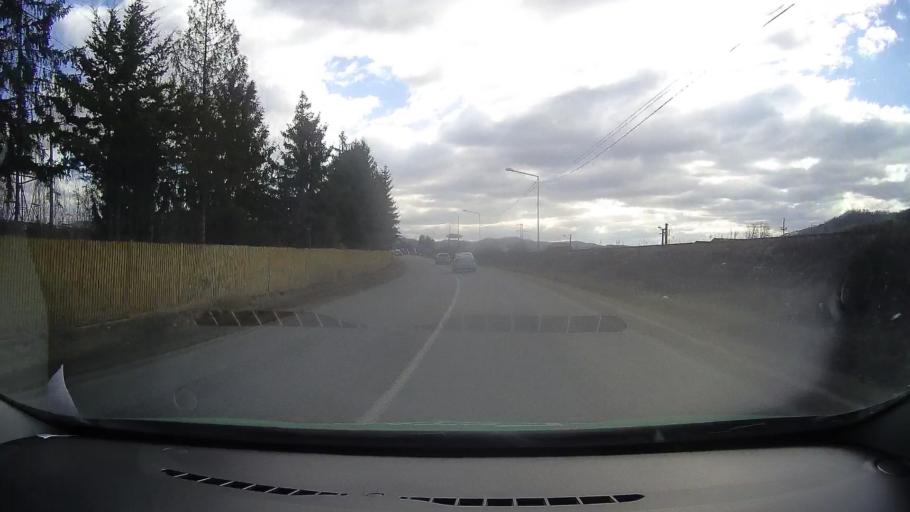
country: RO
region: Dambovita
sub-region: Oras Pucioasa
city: Pucioasa
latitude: 45.0836
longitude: 25.4219
